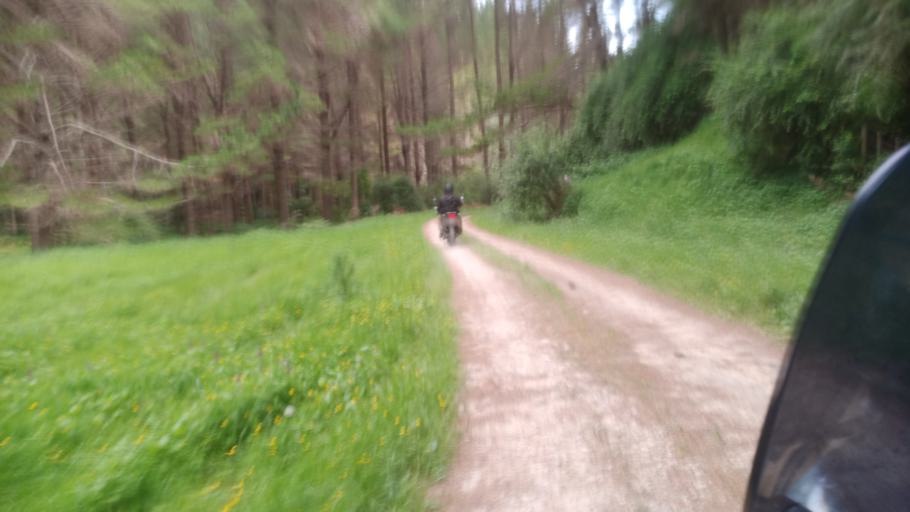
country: NZ
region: Gisborne
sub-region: Gisborne District
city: Gisborne
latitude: -38.4596
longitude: 177.9095
